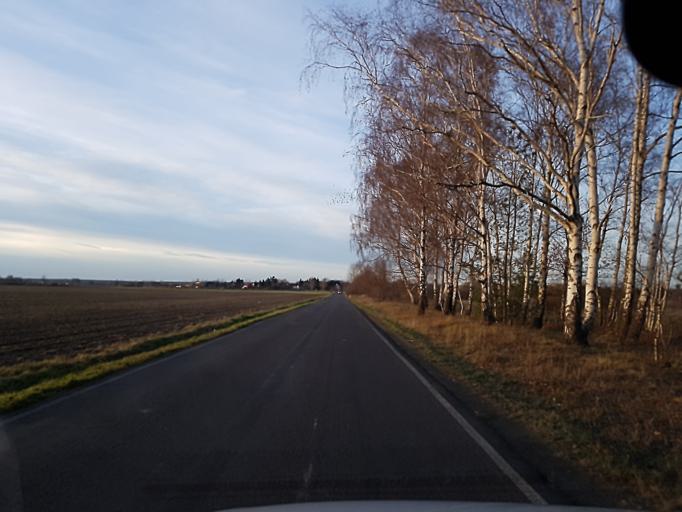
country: DE
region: Brandenburg
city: Finsterwalde
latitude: 51.6050
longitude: 13.7231
